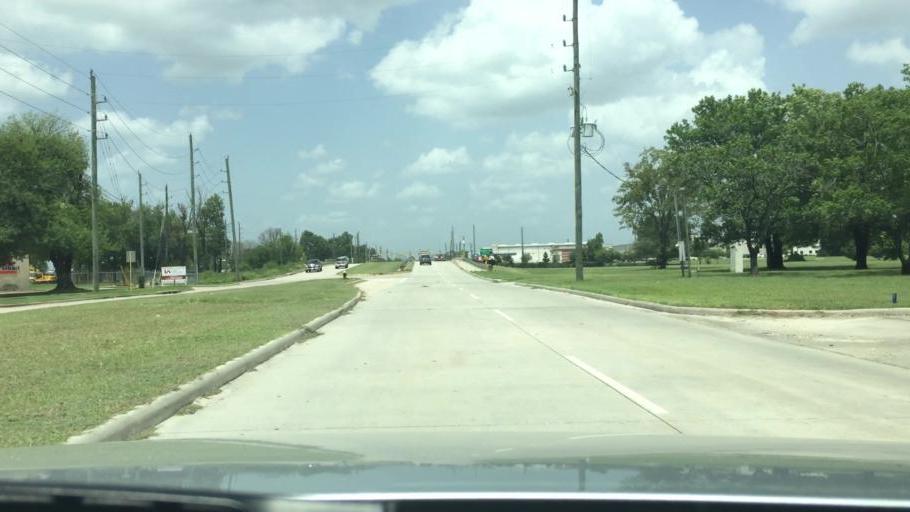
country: US
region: Texas
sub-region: Harris County
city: Hudson
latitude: 29.9476
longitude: -95.5185
